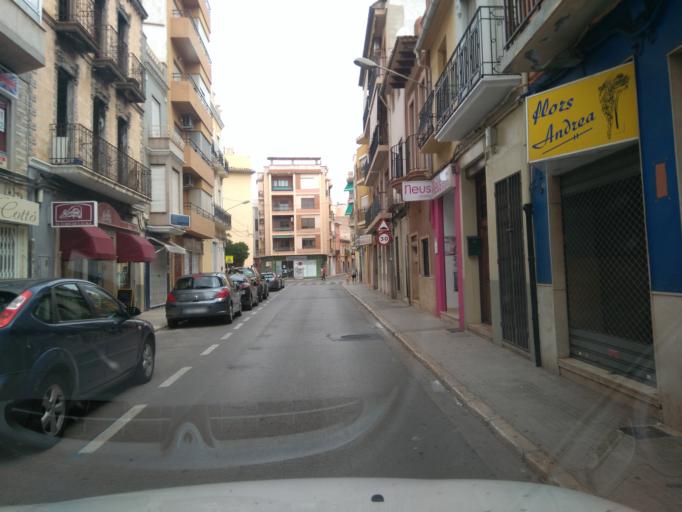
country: ES
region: Valencia
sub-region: Provincia de Valencia
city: Carcaixent
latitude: 39.1213
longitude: -0.4481
